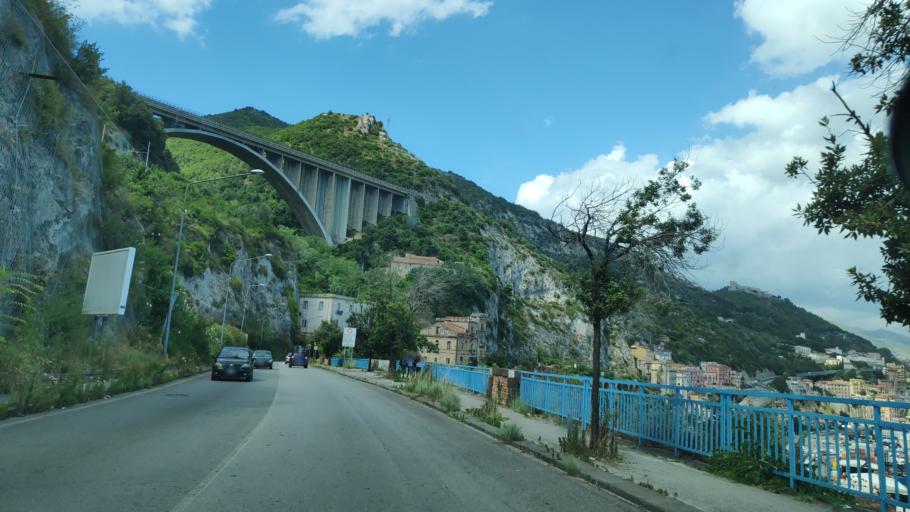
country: IT
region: Campania
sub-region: Provincia di Salerno
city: Vietri sul Mare
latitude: 40.6743
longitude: 14.7365
